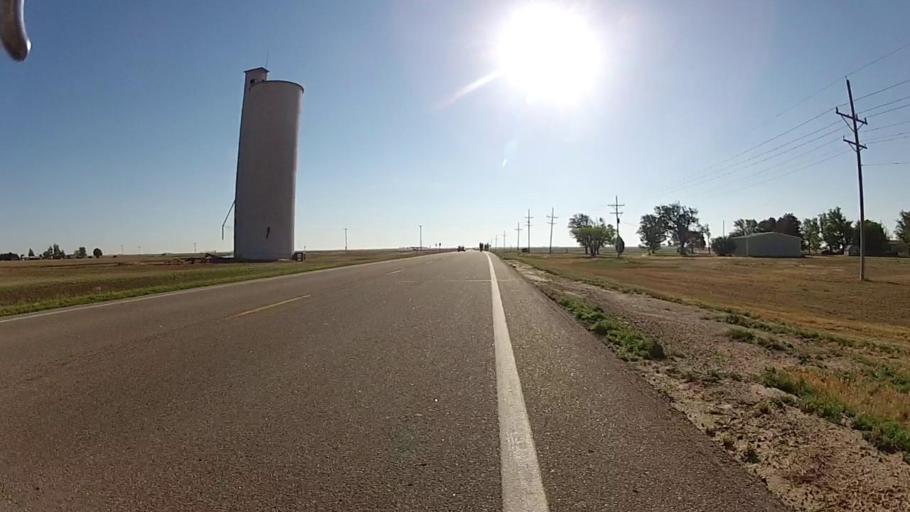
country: US
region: Kansas
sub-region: Haskell County
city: Sublette
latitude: 37.5156
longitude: -100.7272
